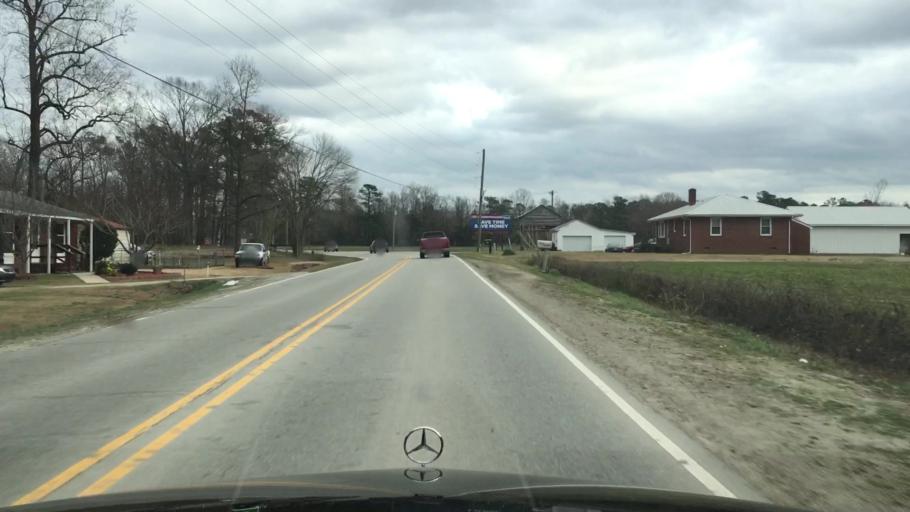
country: US
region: North Carolina
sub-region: Onslow County
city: Richlands
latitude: 34.8786
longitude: -77.5178
